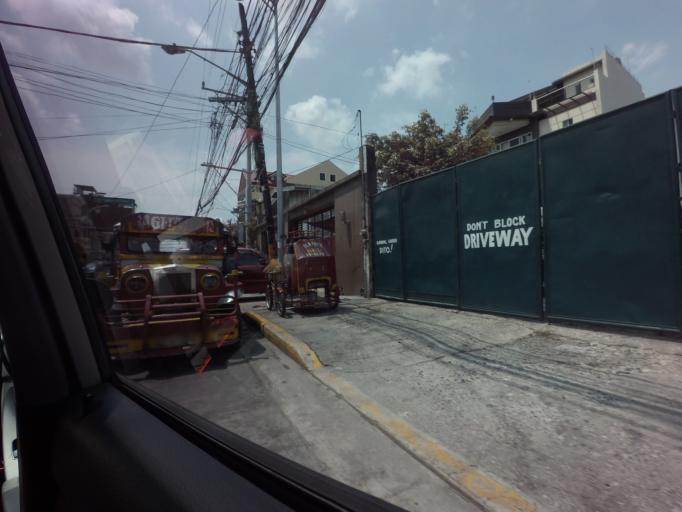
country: PH
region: Metro Manila
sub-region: City of Manila
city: Quiapo
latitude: 14.5857
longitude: 121.0035
